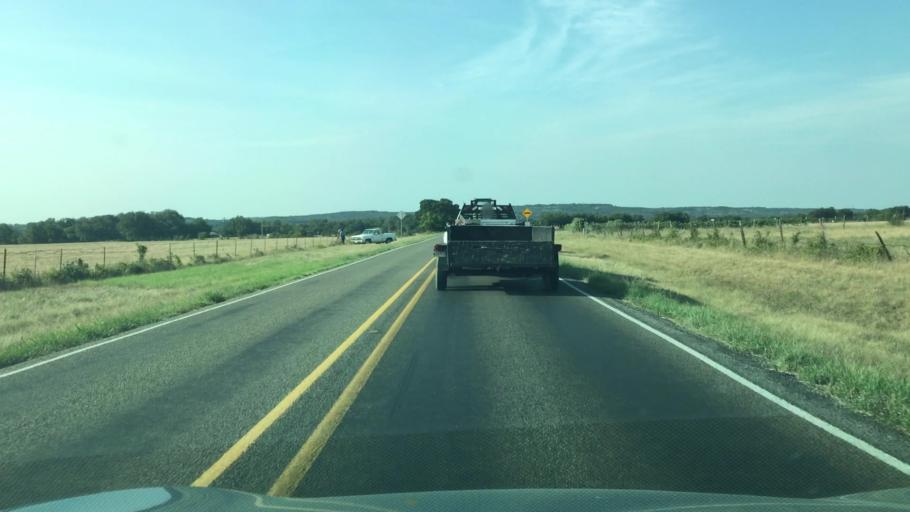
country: US
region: Texas
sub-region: Hays County
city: Dripping Springs
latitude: 30.1915
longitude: -98.2150
